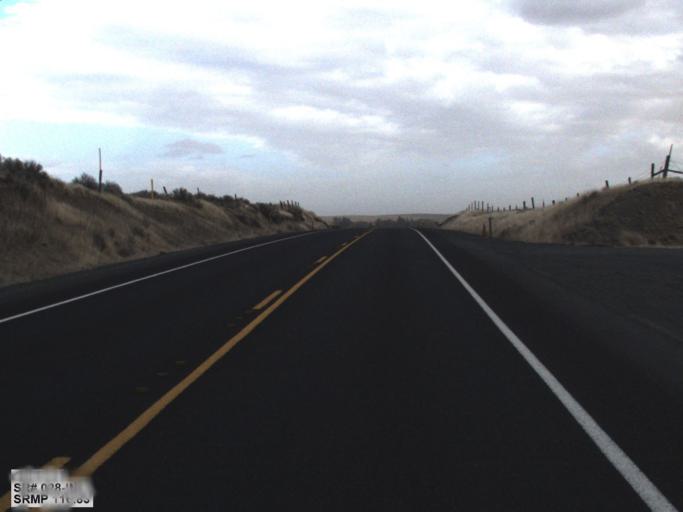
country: US
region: Washington
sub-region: Lincoln County
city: Davenport
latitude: 47.4753
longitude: -118.2760
